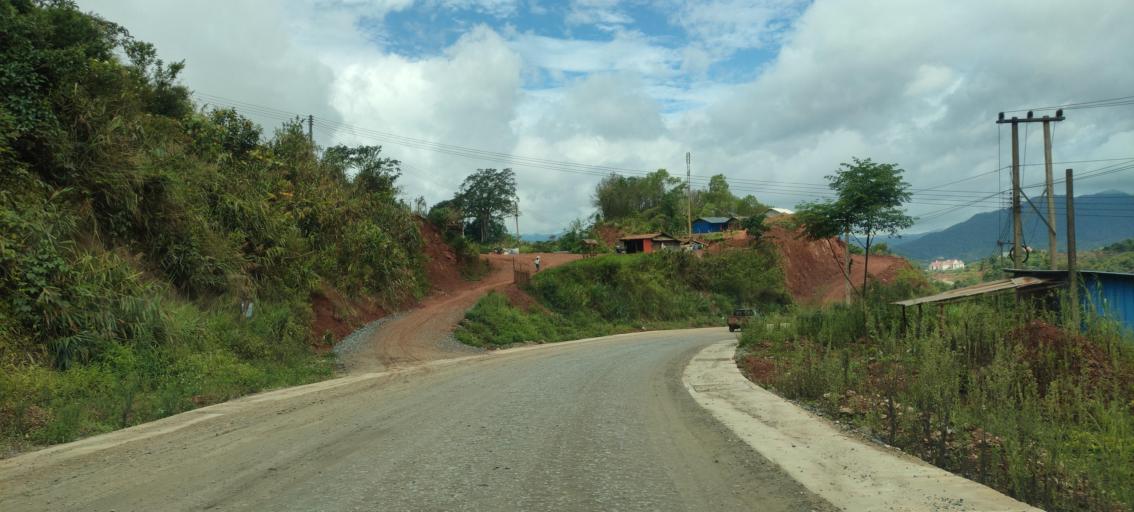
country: LA
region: Phongsali
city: Phongsali
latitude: 21.6324
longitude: 101.9242
